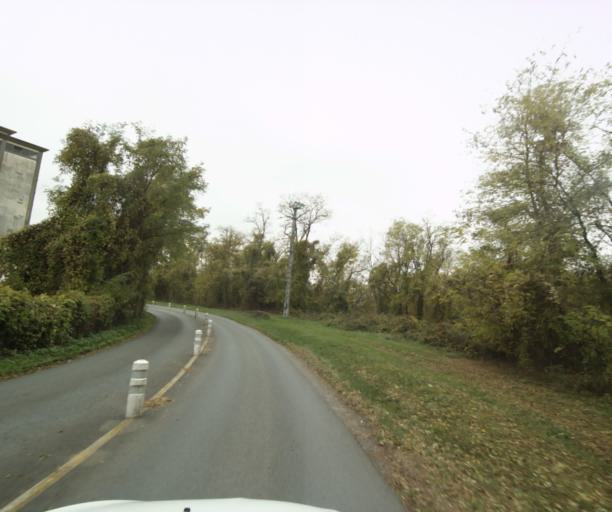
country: FR
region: Poitou-Charentes
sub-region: Departement de la Charente-Maritime
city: Saintes
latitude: 45.7586
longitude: -0.6179
